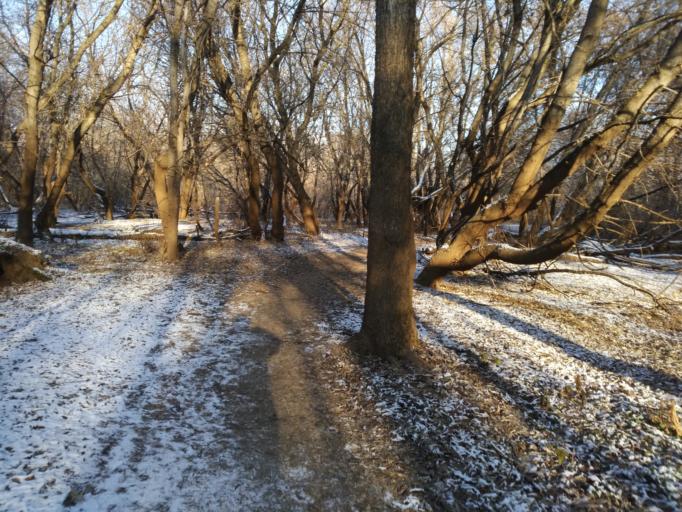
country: RU
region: Kirov
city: Vyatskiye Polyany
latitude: 56.2375
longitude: 51.0797
